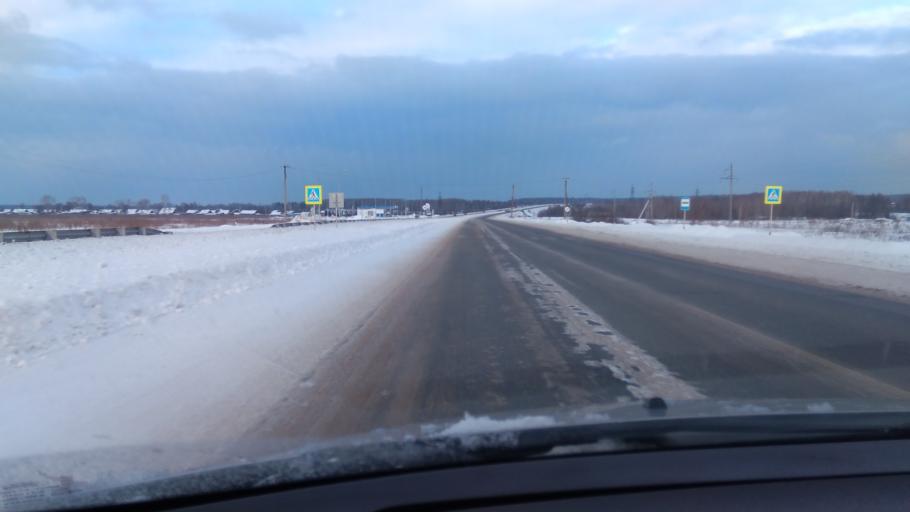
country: RU
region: Sverdlovsk
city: Tsementnyy
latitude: 57.4937
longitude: 60.1766
